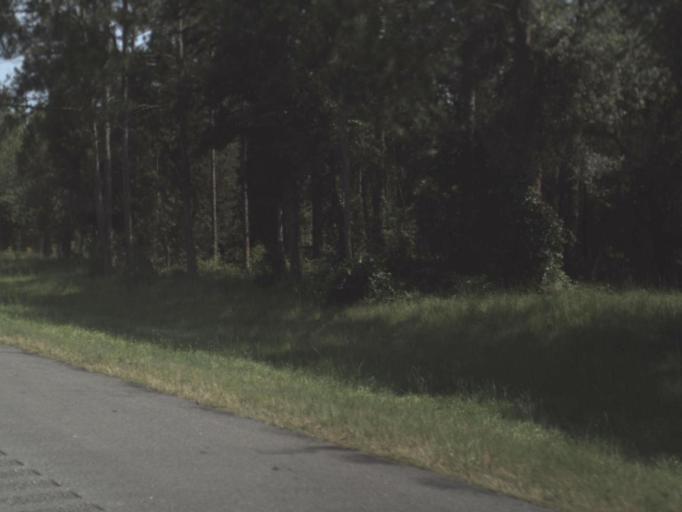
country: US
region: Florida
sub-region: Suwannee County
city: Wellborn
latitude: 30.3542
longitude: -82.8388
